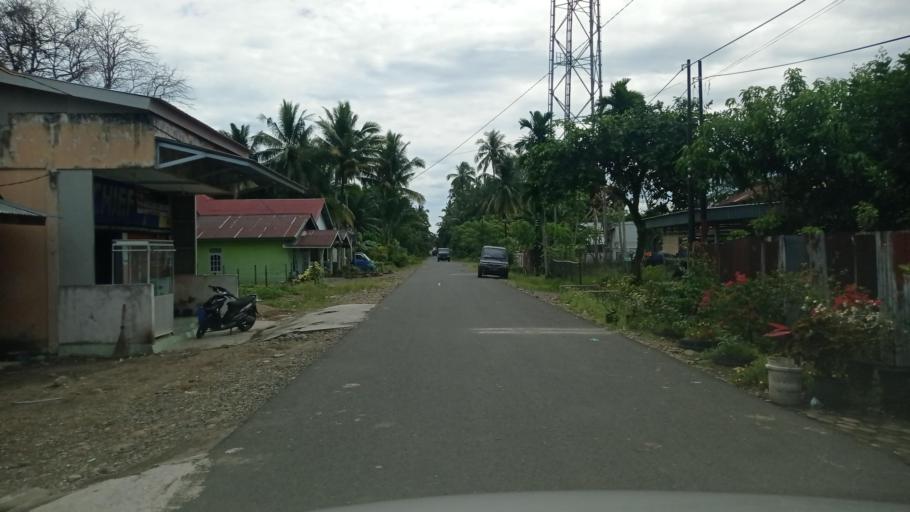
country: ID
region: Bengkulu
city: Ipuh
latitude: -2.5803
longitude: 101.1171
